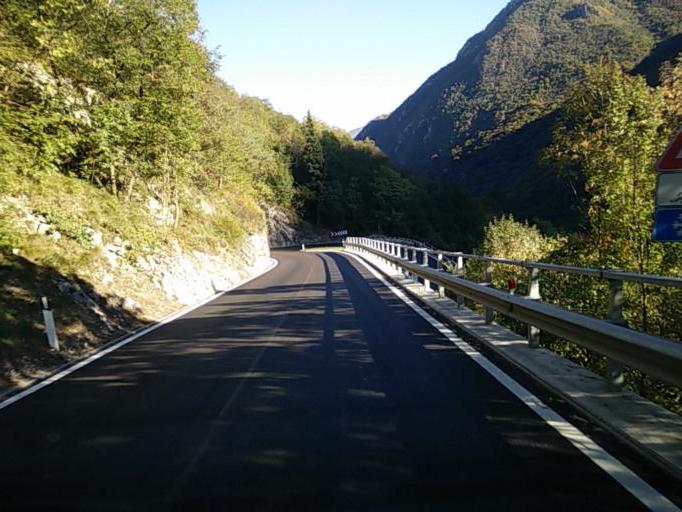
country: IT
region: Trentino-Alto Adige
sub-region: Provincia di Trento
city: Molina di Ledro
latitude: 45.8683
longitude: 10.7908
